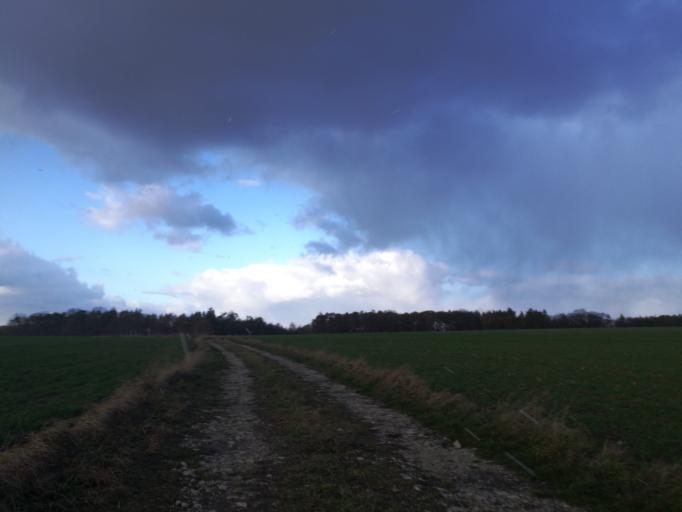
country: DE
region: Bavaria
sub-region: Regierungsbezirk Mittelfranken
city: Obermichelbach
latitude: 49.4997
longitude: 10.9259
